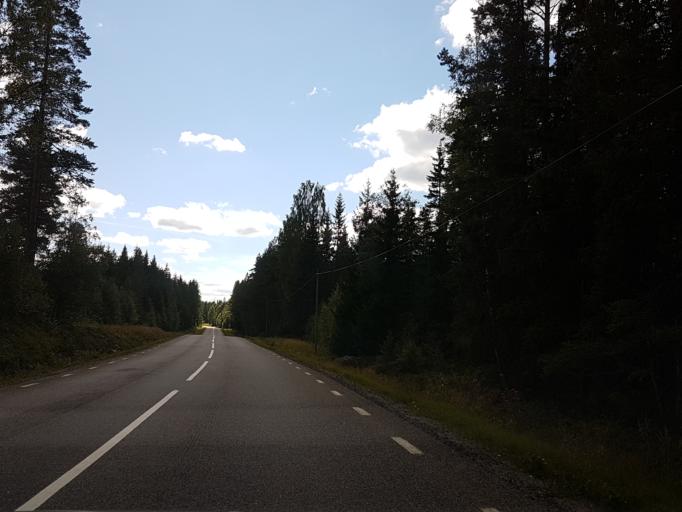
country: SE
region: Vaesterbotten
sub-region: Umea Kommun
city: Saevar
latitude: 64.1288
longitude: 20.5476
